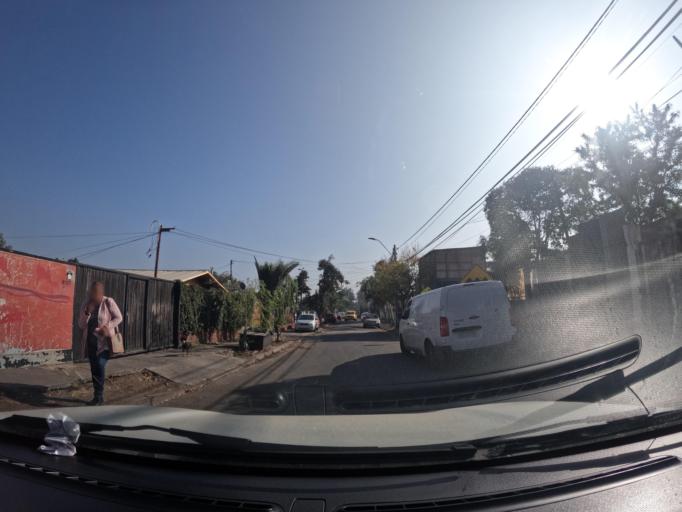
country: CL
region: Santiago Metropolitan
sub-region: Provincia de Santiago
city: Villa Presidente Frei, Nunoa, Santiago, Chile
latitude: -33.4712
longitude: -70.5267
